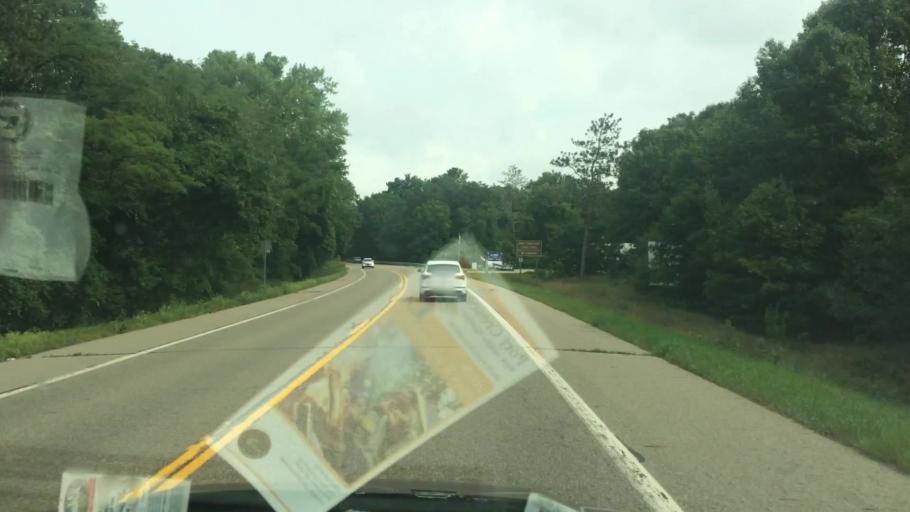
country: US
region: Michigan
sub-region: Huron County
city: Bad Axe
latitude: 44.0045
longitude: -83.0527
